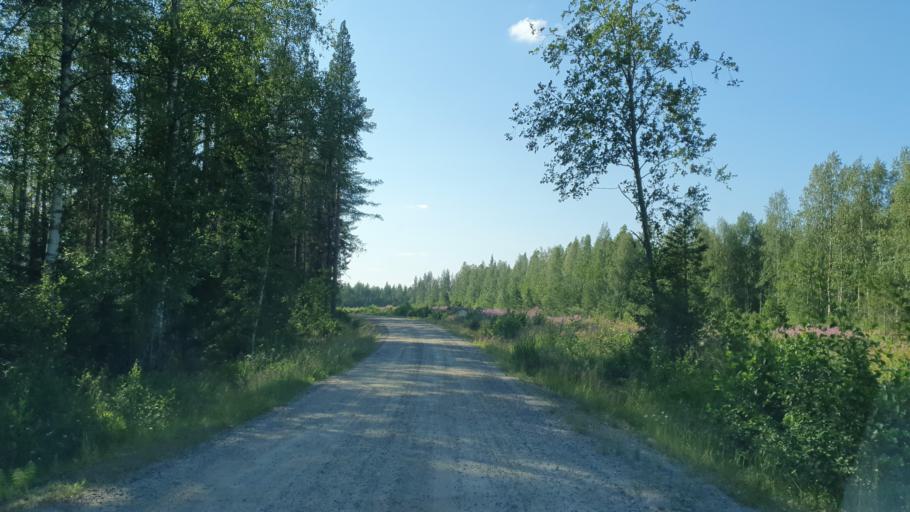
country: FI
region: Kainuu
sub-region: Kehys-Kainuu
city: Kuhmo
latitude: 64.0181
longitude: 29.7501
